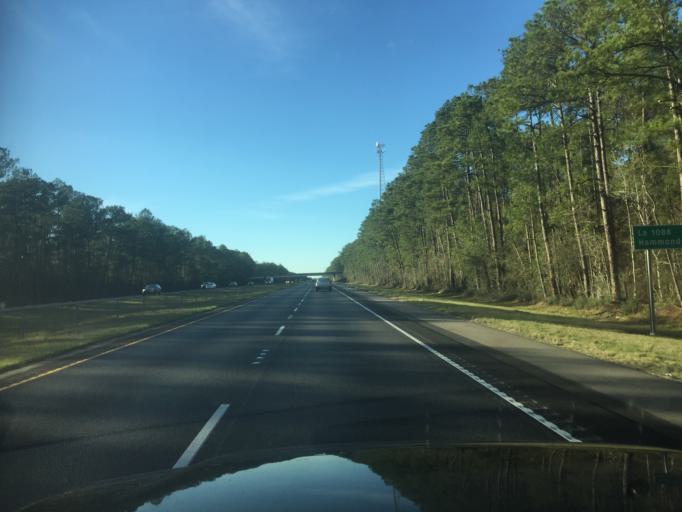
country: US
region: Louisiana
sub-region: Saint Tammany Parish
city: Lacombe
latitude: 30.3594
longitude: -89.9336
